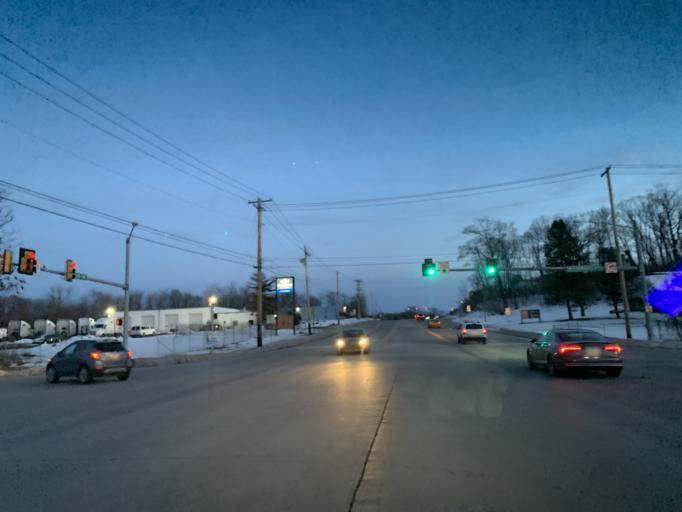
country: US
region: Pennsylvania
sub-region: Cumberland County
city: Carlisle
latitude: 40.1831
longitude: -77.2370
